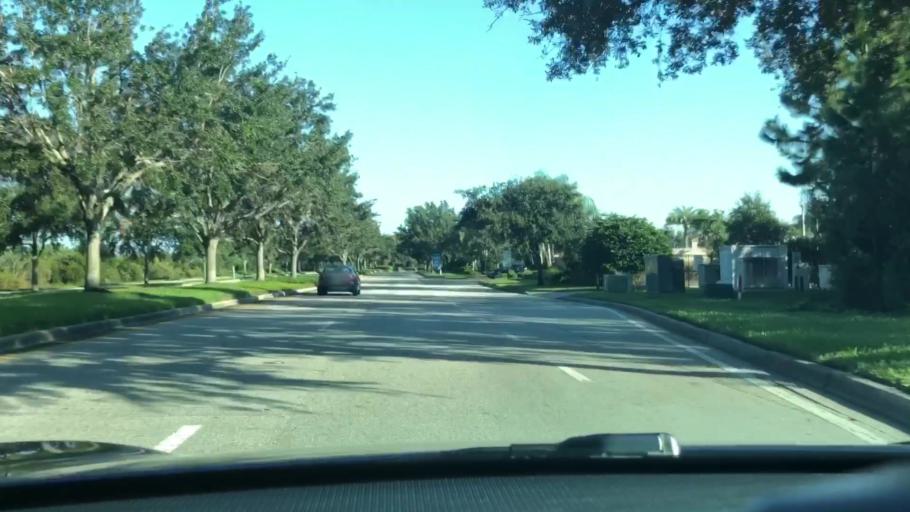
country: US
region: Florida
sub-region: Orange County
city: Meadow Woods
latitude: 28.3891
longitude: -81.2759
